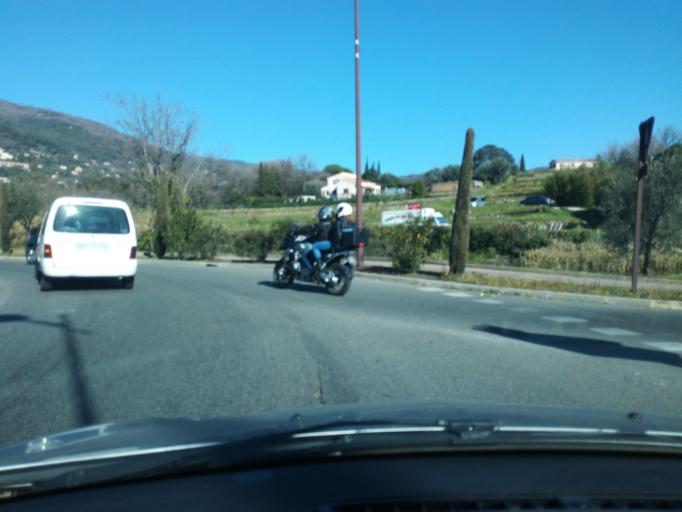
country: FR
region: Provence-Alpes-Cote d'Azur
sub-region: Departement des Alpes-Maritimes
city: Grasse
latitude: 43.6537
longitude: 6.9449
